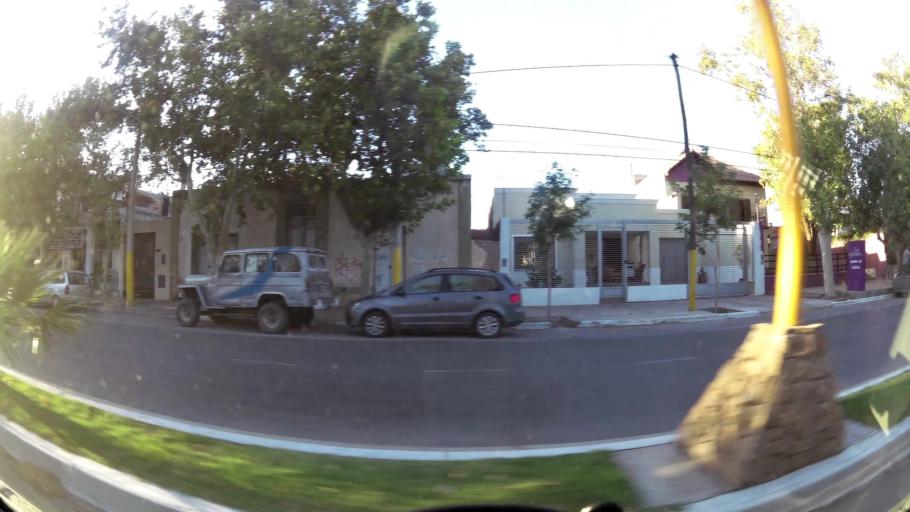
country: AR
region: San Juan
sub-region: Departamento de Santa Lucia
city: Santa Lucia
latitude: -31.5414
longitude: -68.5013
